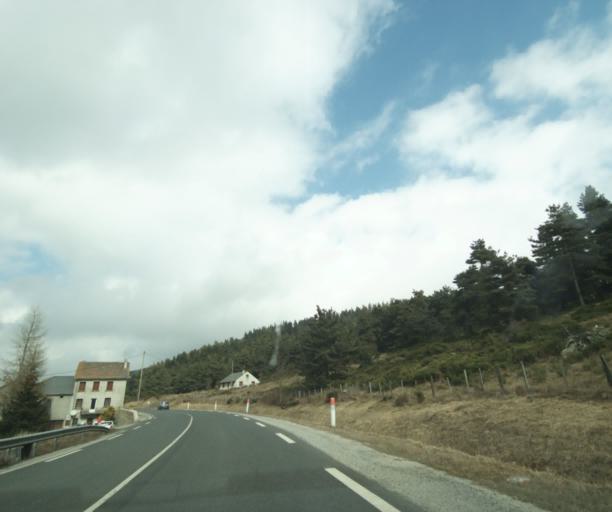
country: FR
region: Languedoc-Roussillon
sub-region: Departement de la Lozere
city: Mende
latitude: 44.6058
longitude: 3.6753
